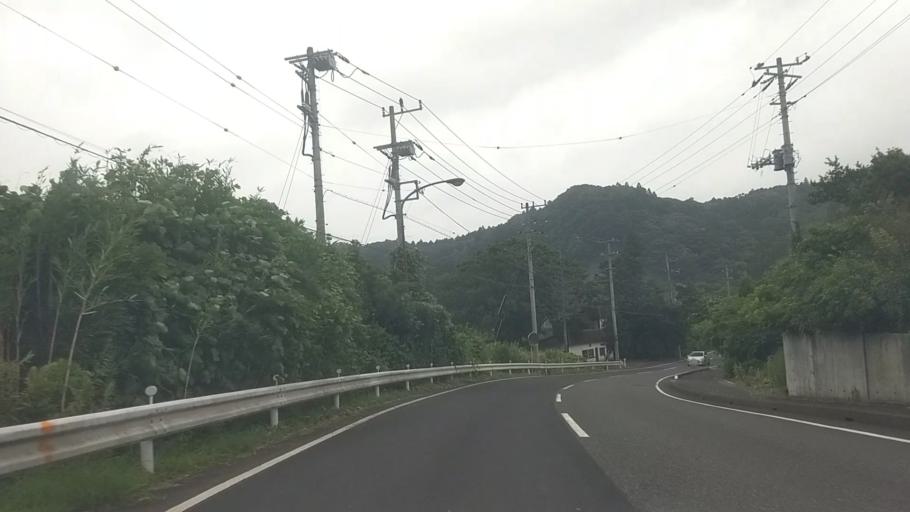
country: JP
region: Chiba
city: Ohara
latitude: 35.2683
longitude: 140.2540
